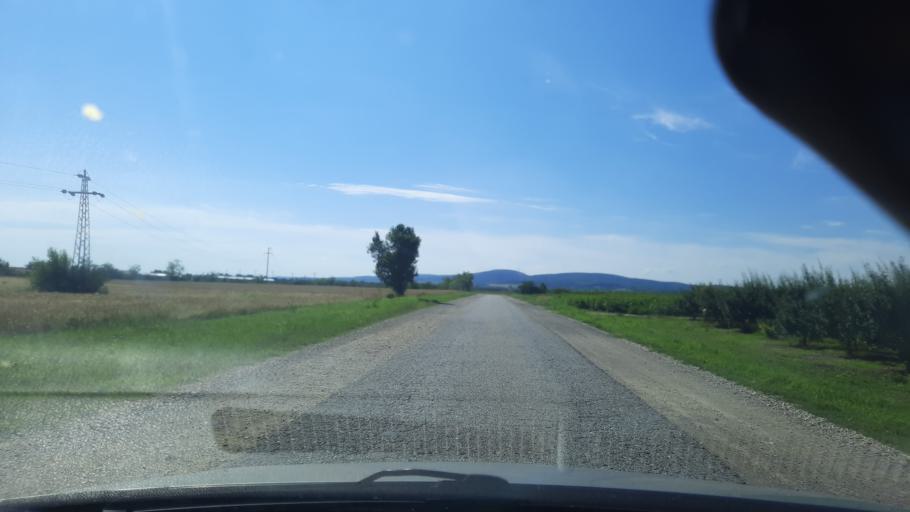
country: RS
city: Cortanovci
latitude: 45.1133
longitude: 19.9656
